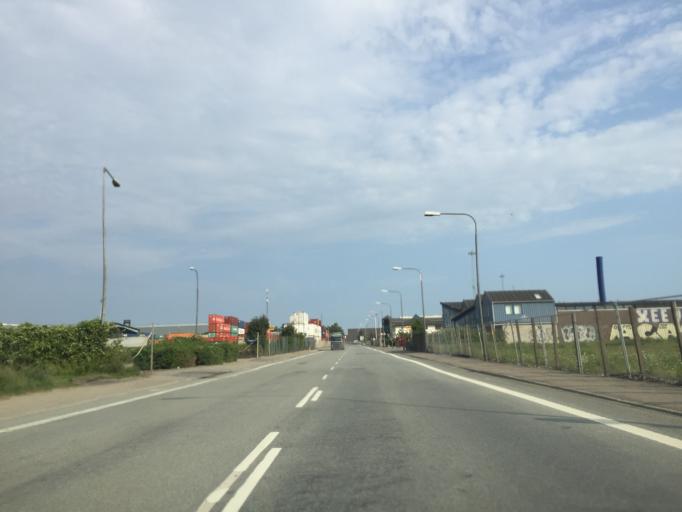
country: DK
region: Capital Region
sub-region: Gentofte Kommune
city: Charlottenlund
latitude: 55.7179
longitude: 12.5986
